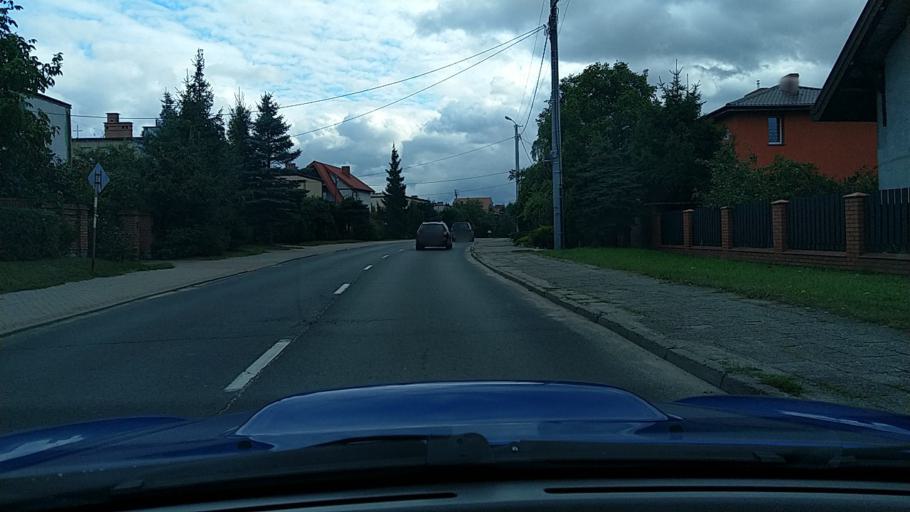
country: PL
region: Warmian-Masurian Voivodeship
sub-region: Olsztyn
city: Kortowo
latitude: 53.7675
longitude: 20.4277
